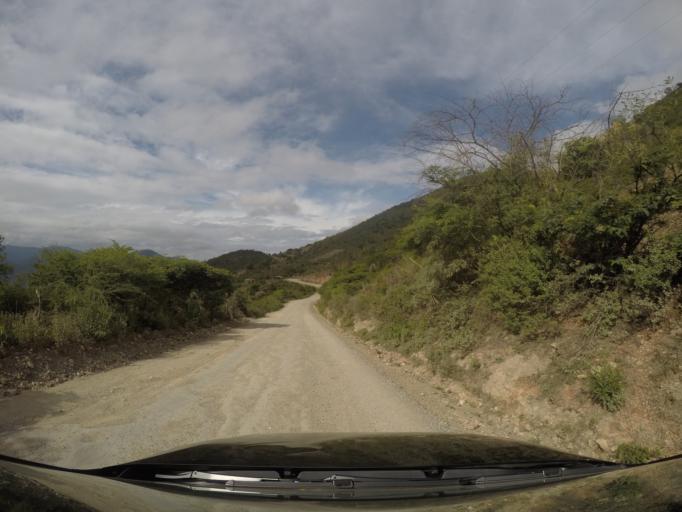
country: MX
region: Oaxaca
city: San Lorenzo Albarradas
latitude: 16.8893
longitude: -96.2648
